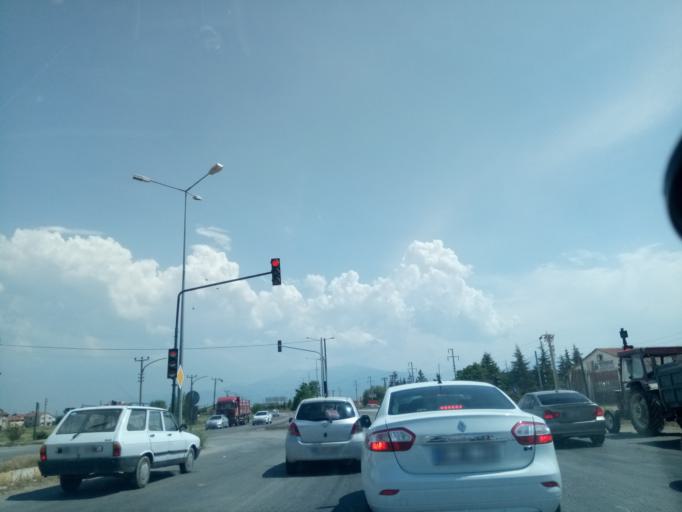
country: TR
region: Afyonkarahisar
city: Bolvadin
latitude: 38.7065
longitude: 31.0343
